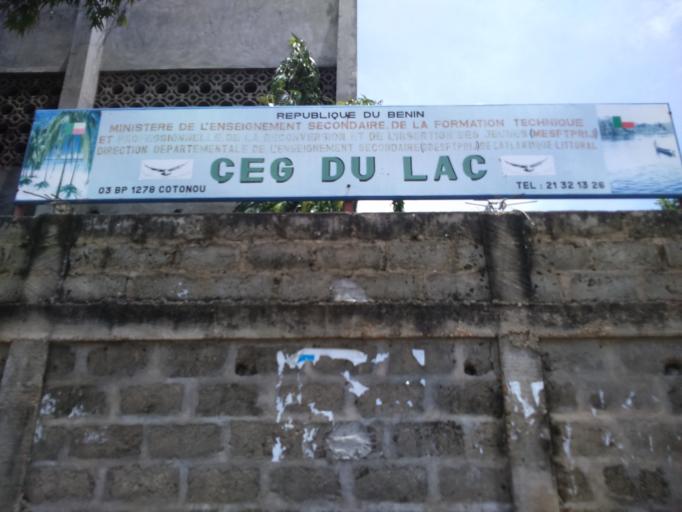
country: BJ
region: Littoral
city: Cotonou
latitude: 6.3869
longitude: 2.4221
